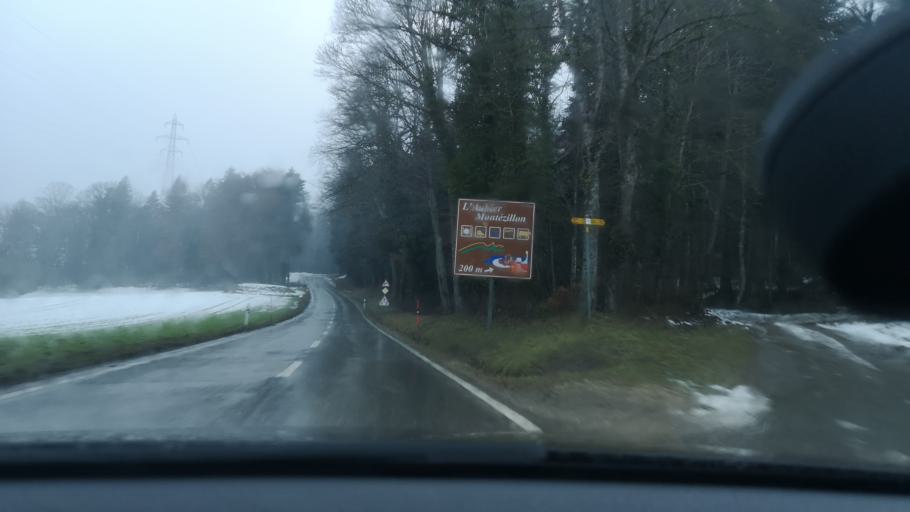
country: CH
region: Neuchatel
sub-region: Val-de-Ruz District
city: Les Geneveys-sur-Coffrane
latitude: 46.9840
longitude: 6.8464
